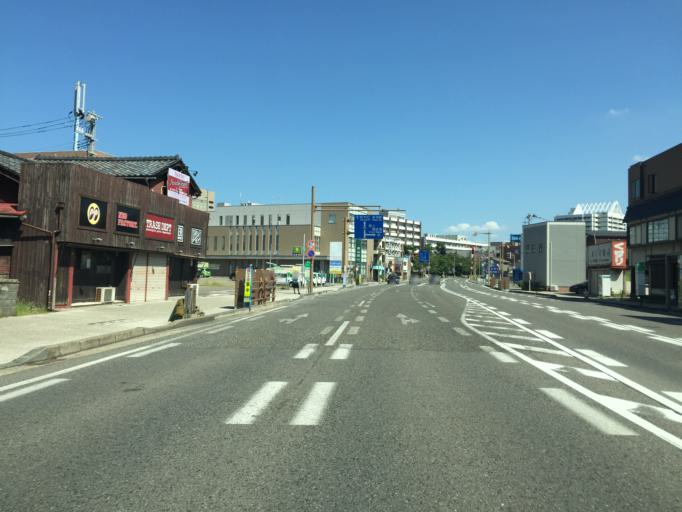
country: JP
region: Niigata
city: Niigata-shi
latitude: 37.9170
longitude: 139.0320
